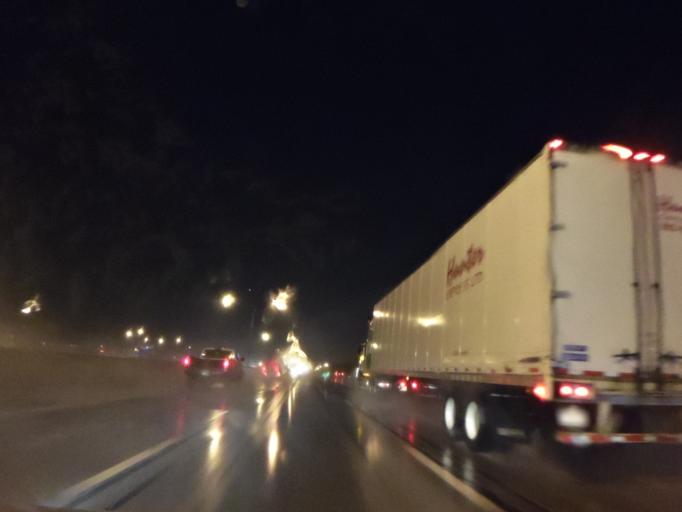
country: US
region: Kentucky
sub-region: Boone County
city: Union
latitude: 38.9361
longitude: -84.6316
